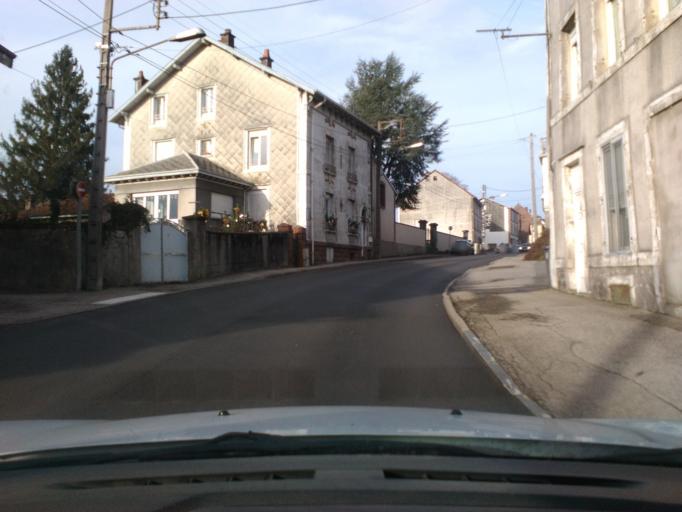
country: FR
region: Lorraine
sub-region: Departement des Vosges
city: Bruyeres
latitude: 48.2060
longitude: 6.7218
